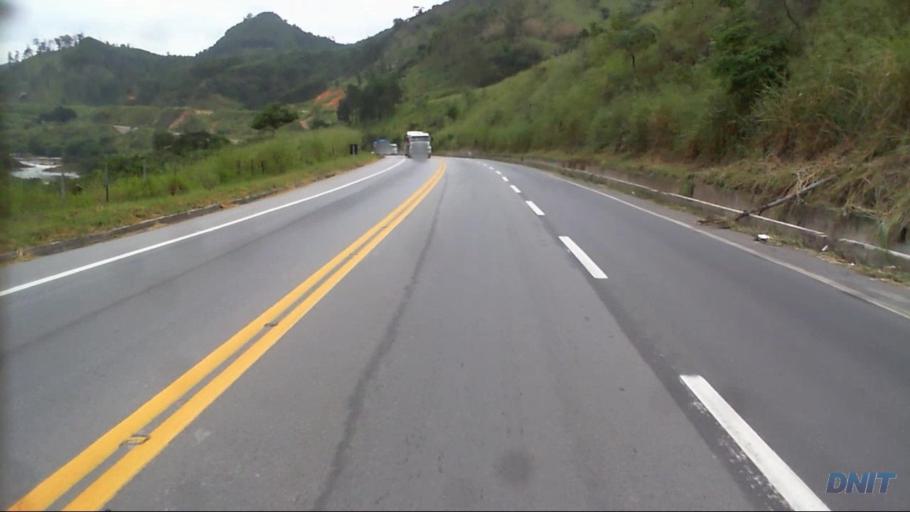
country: BR
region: Minas Gerais
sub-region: Timoteo
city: Timoteo
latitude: -19.6196
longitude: -42.8011
